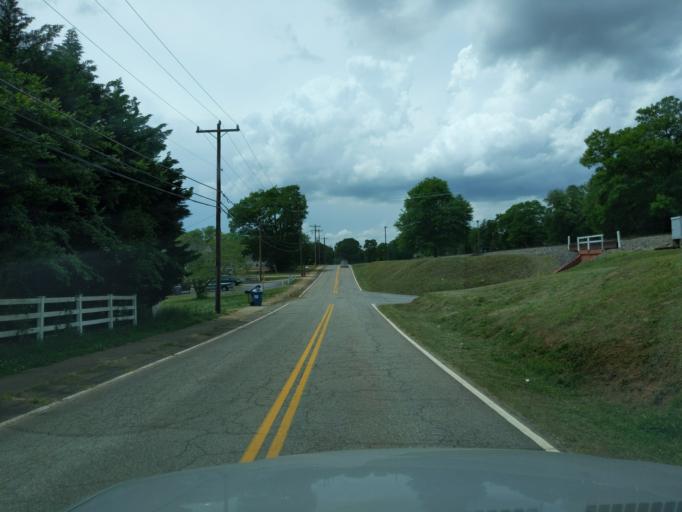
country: US
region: South Carolina
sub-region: Spartanburg County
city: Wellford
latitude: 34.9535
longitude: -82.0958
